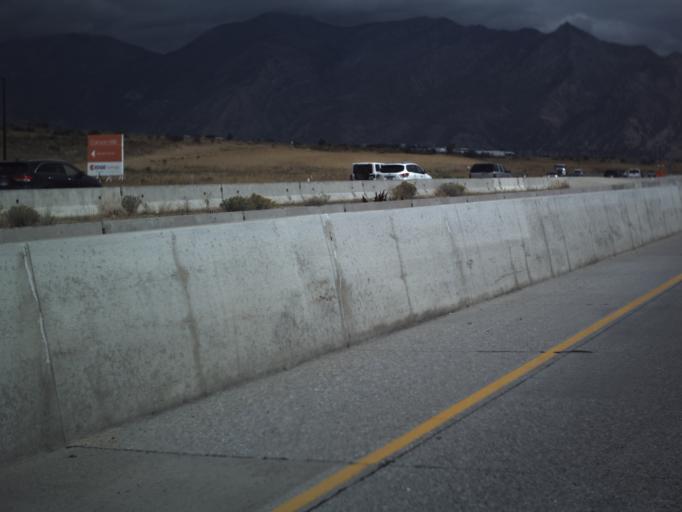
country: US
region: Utah
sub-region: Utah County
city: Lehi
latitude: 40.4322
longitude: -111.8580
